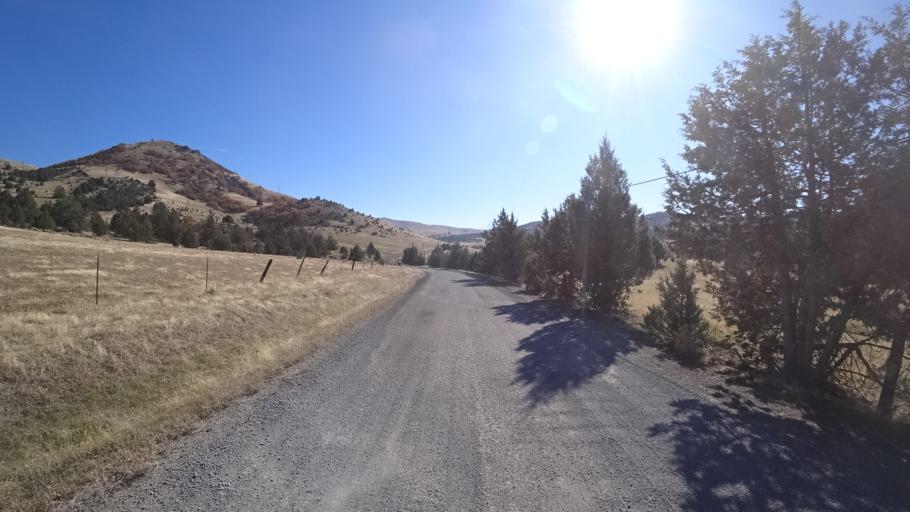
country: US
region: California
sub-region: Siskiyou County
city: Montague
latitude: 41.8025
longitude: -122.3700
